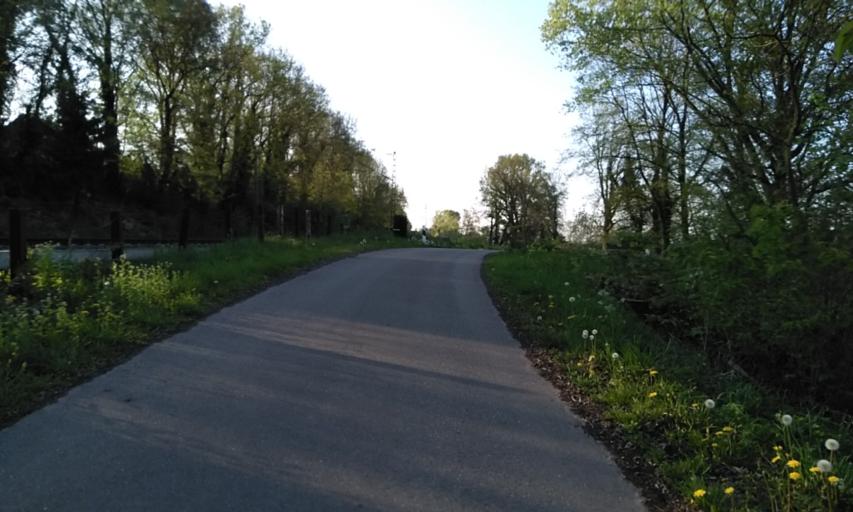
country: DE
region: Lower Saxony
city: Dollern
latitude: 53.5401
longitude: 9.5616
